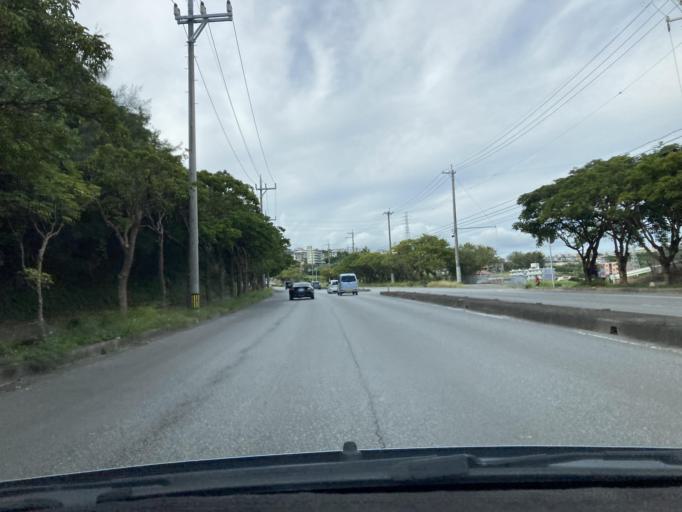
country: JP
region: Okinawa
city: Gushikawa
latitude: 26.3420
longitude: 127.8429
